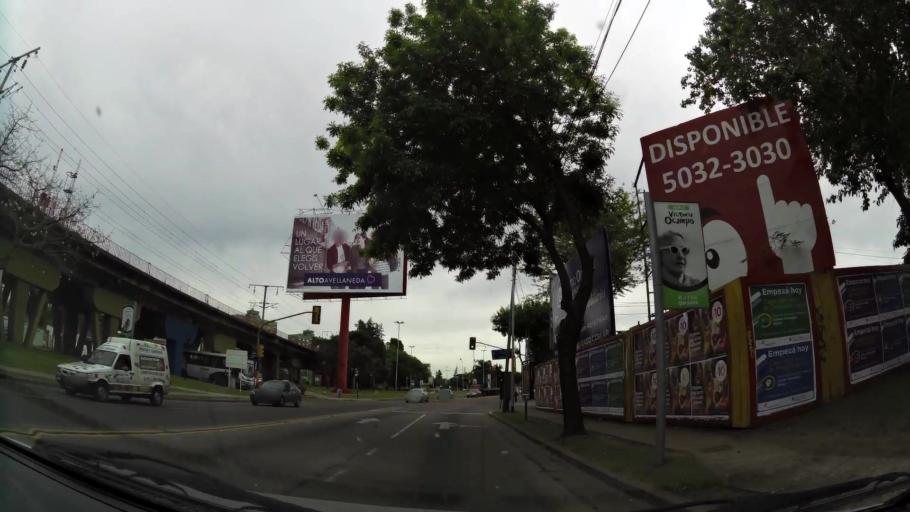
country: AR
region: Buenos Aires
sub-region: Partido de Avellaneda
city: Avellaneda
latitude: -34.6733
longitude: -58.3602
